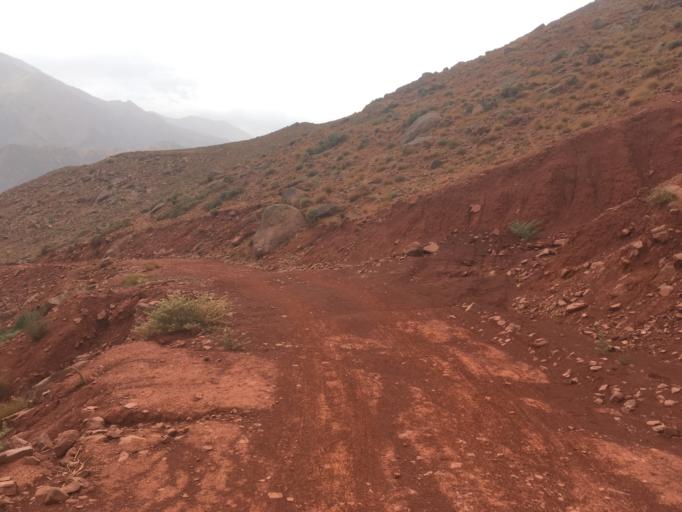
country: MA
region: Marrakech-Tensift-Al Haouz
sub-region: Al-Haouz
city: Tidili Mesfioua
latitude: 31.2801
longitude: -7.6750
